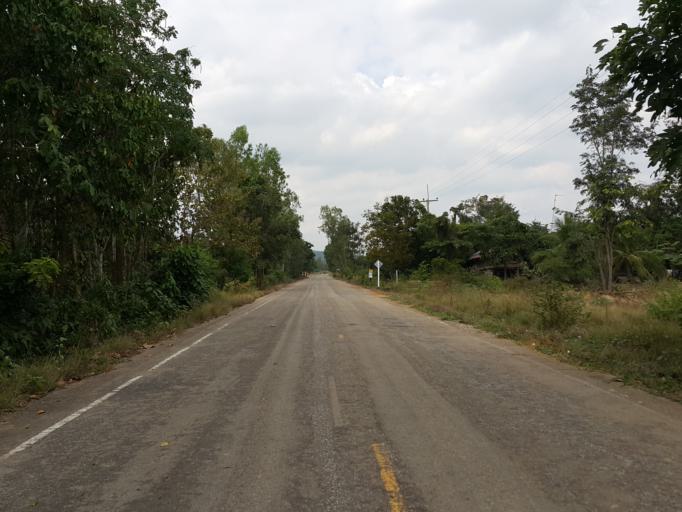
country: TH
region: Sukhothai
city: Thung Saliam
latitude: 17.3779
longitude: 99.5895
